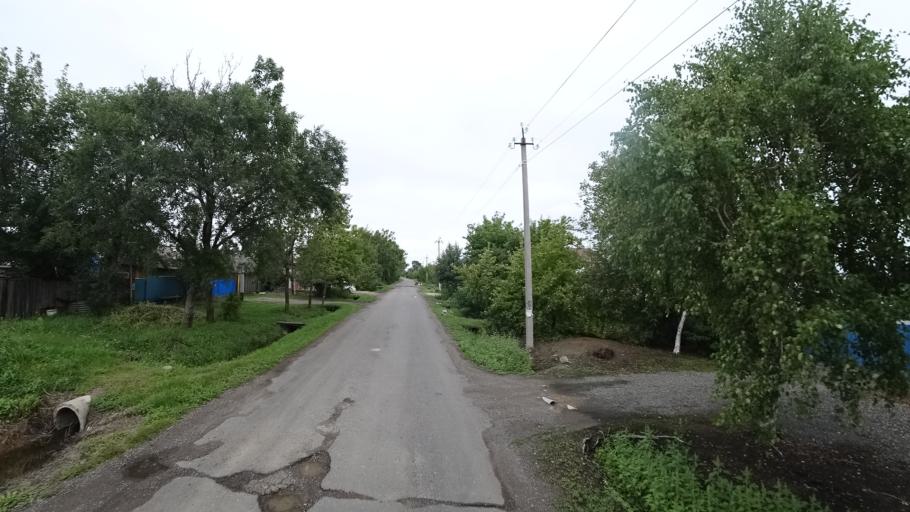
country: RU
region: Primorskiy
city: Chernigovka
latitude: 44.3415
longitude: 132.5870
